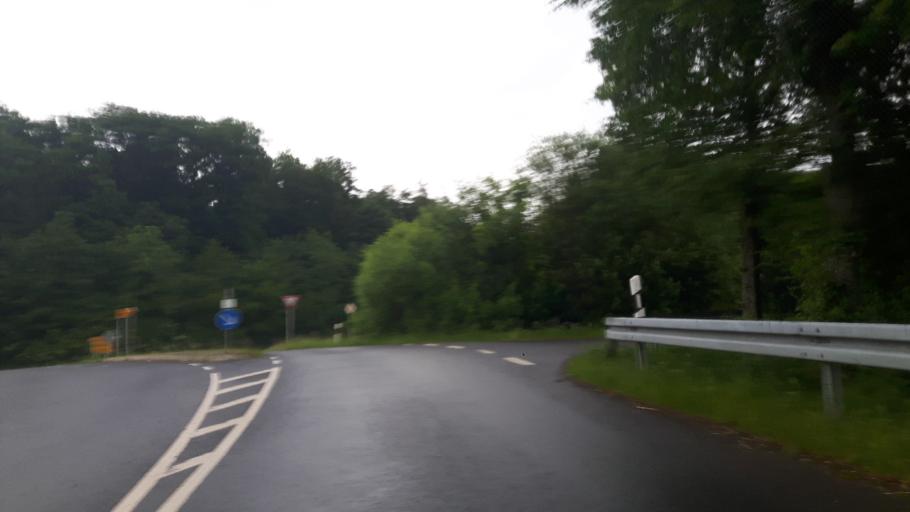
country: DE
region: Bavaria
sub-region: Regierungsbezirk Unterfranken
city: Uchtelhausen
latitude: 50.1216
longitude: 10.3017
